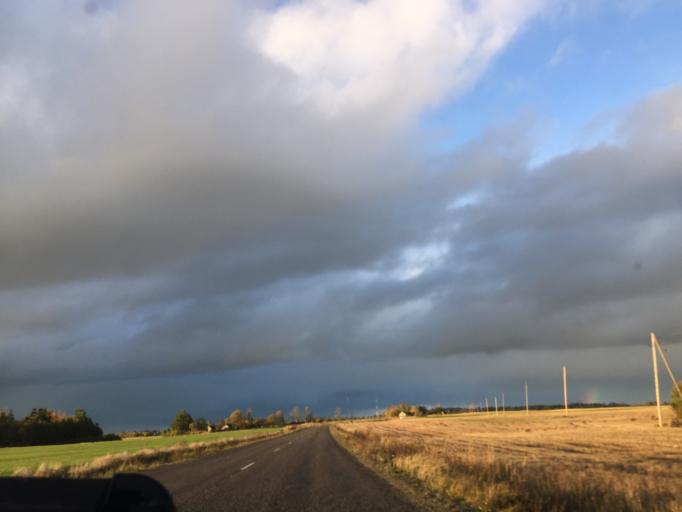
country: LV
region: Talsu Rajons
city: Sabile
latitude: 56.9257
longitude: 22.3961
